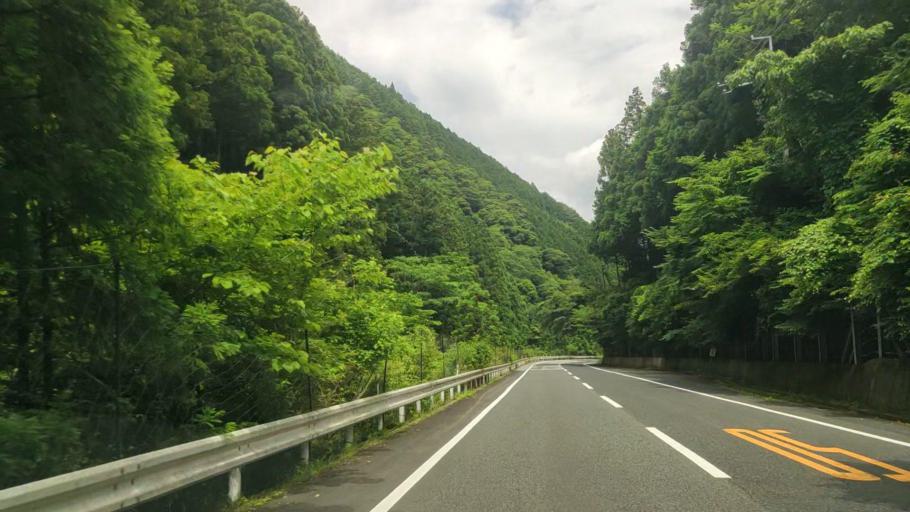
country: JP
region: Kyoto
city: Fukuchiyama
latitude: 35.2247
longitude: 134.9521
